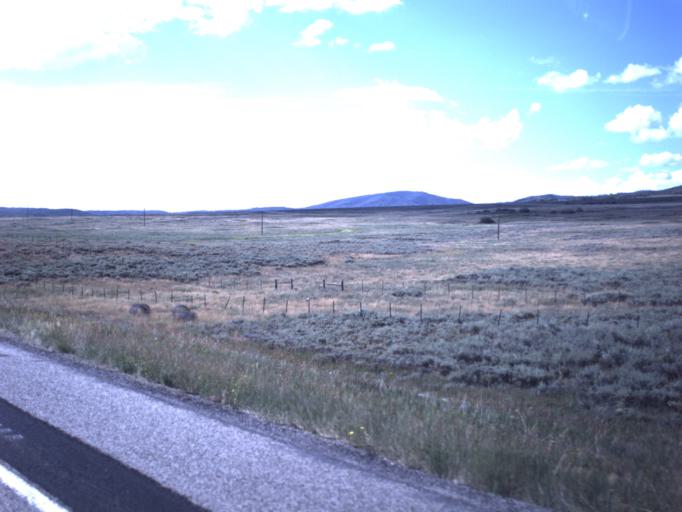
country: US
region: Utah
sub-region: Wasatch County
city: Heber
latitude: 40.2382
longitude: -111.1404
